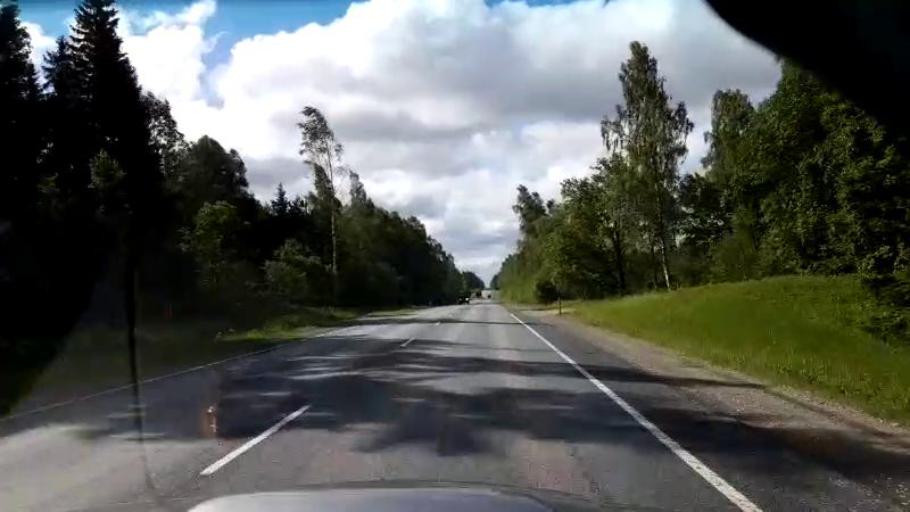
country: EE
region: Harju
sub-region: Saue linn
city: Saue
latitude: 59.2209
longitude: 24.4946
